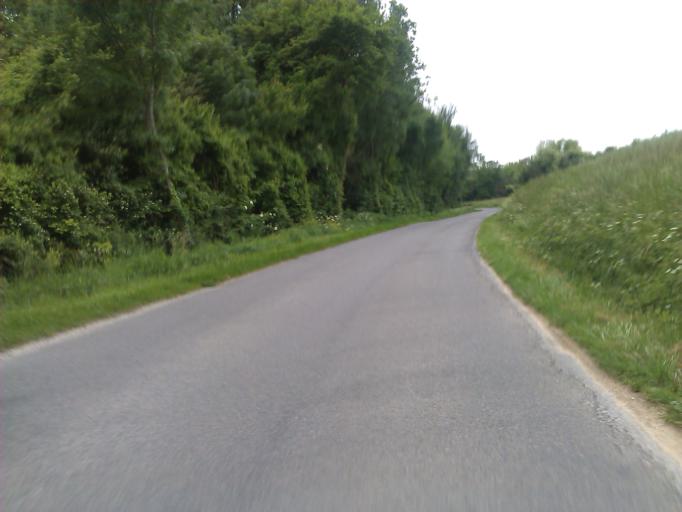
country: FR
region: Poitou-Charentes
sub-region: Departement de la Charente
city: Sireuil
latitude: 45.6380
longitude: 0.0106
